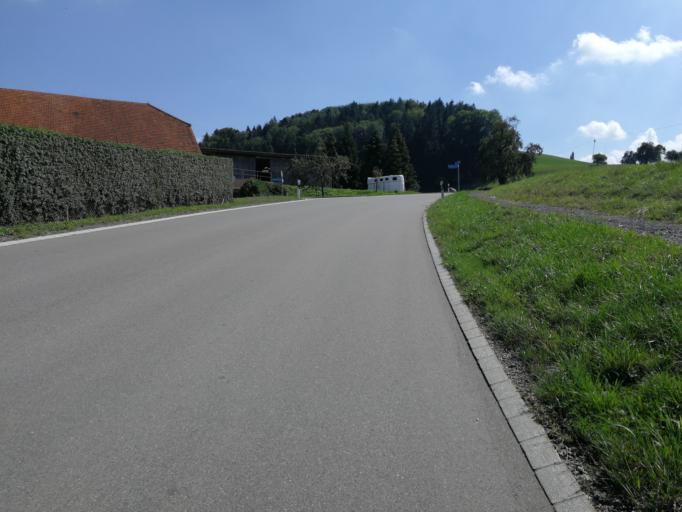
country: CH
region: Zurich
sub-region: Bezirk Horgen
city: Au / Unter-Dorf
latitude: 47.2397
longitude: 8.6271
